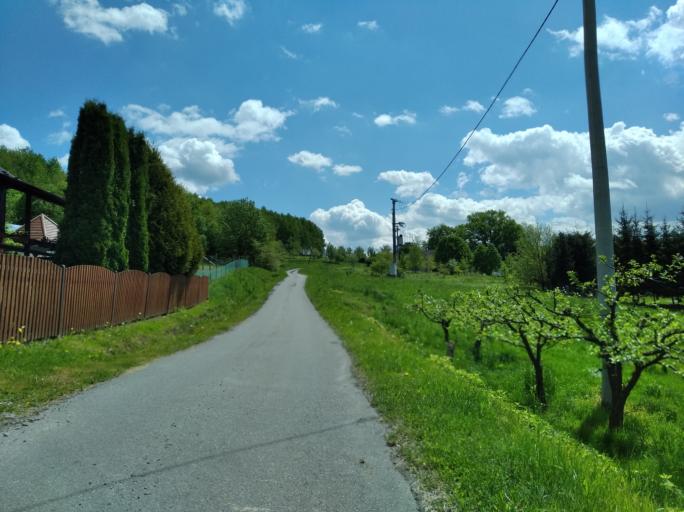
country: PL
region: Subcarpathian Voivodeship
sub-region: Powiat strzyzowski
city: Wisniowa
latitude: 49.8405
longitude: 21.6442
